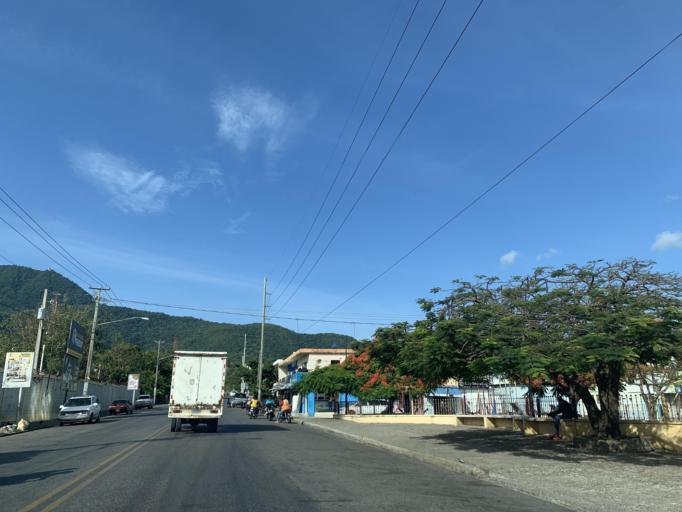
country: DO
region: Puerto Plata
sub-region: Puerto Plata
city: Puerto Plata
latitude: 19.7945
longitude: -70.7030
